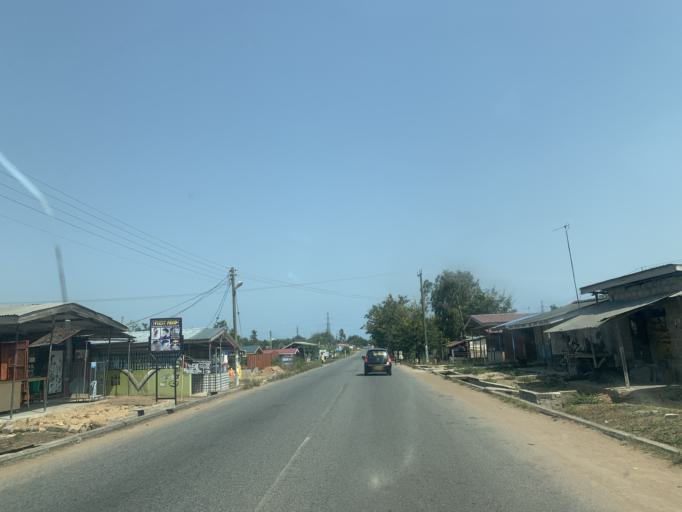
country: GH
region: Central
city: Winneba
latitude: 5.3922
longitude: -0.6468
